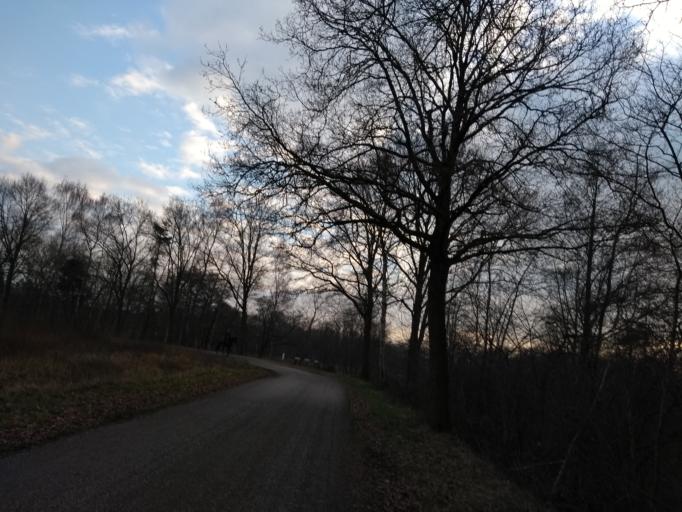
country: NL
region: Overijssel
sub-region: Gemeente Haaksbergen
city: Haaksbergen
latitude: 52.1259
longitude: 6.7585
